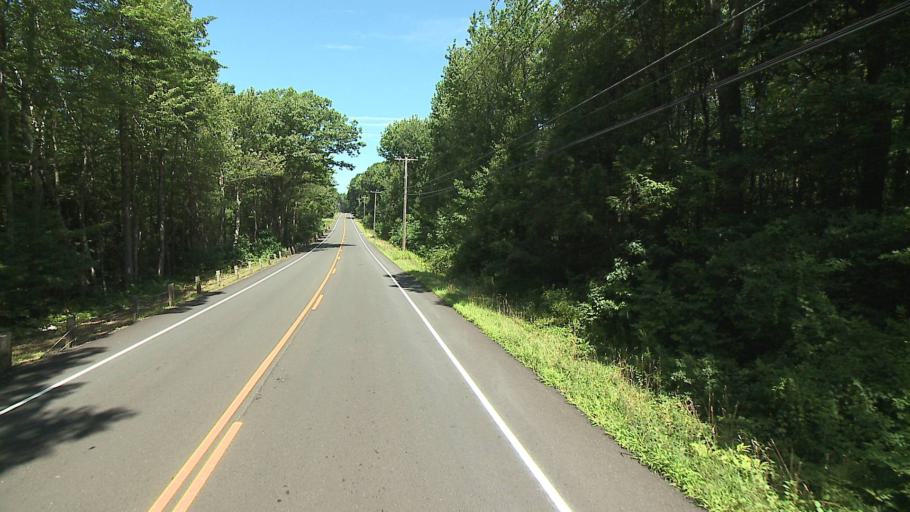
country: US
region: Connecticut
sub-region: Hartford County
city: North Granby
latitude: 41.9563
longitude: -72.9154
